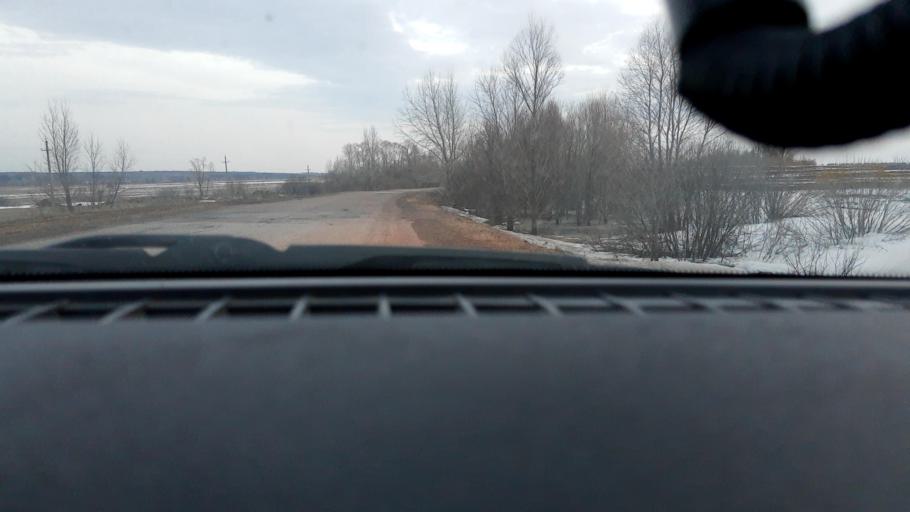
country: RU
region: Bashkortostan
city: Iglino
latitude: 54.6275
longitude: 56.4261
